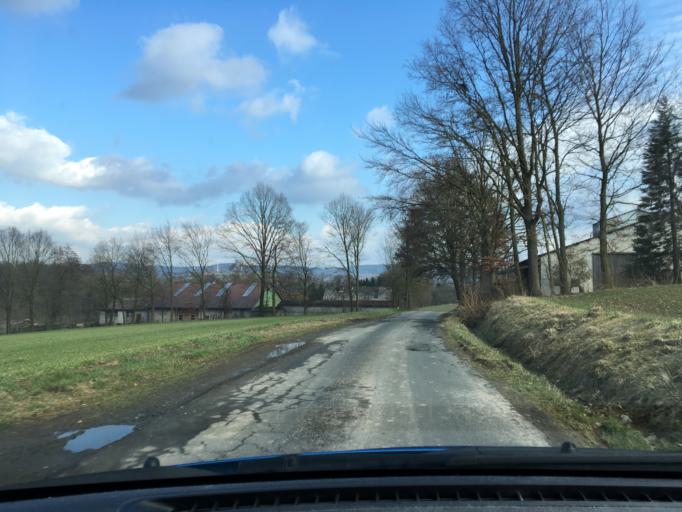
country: DE
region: Lower Saxony
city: Uslar
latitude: 51.6440
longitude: 9.6314
